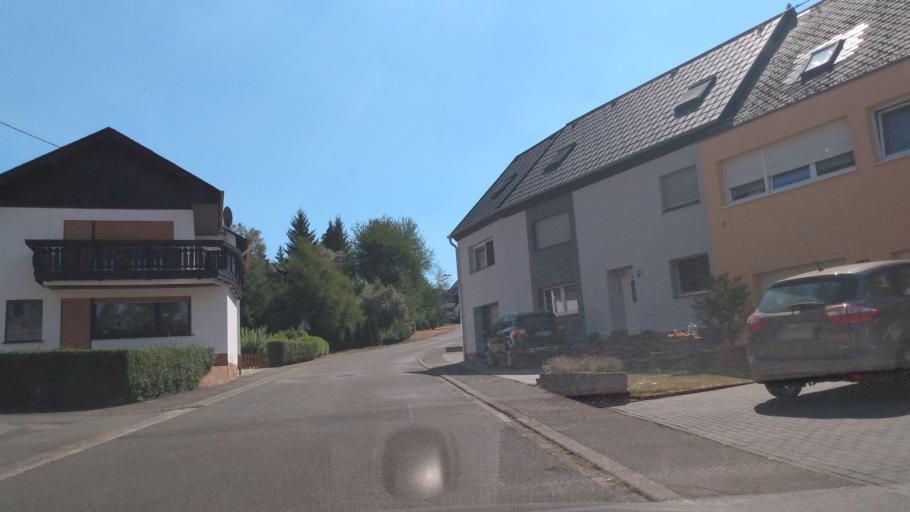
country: DE
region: Rheinland-Pfalz
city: Morbach
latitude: 49.8189
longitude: 7.1486
